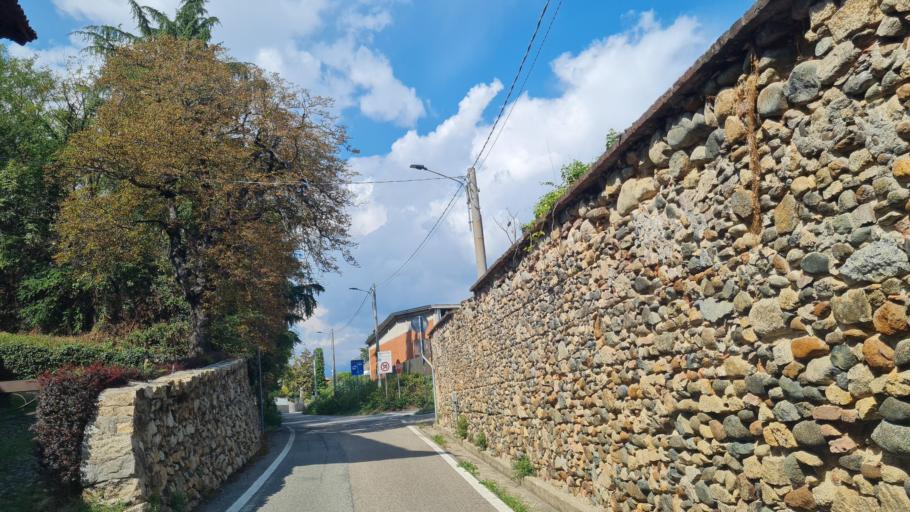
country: IT
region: Piedmont
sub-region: Provincia di Biella
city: Lessona
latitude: 45.5828
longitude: 8.1828
